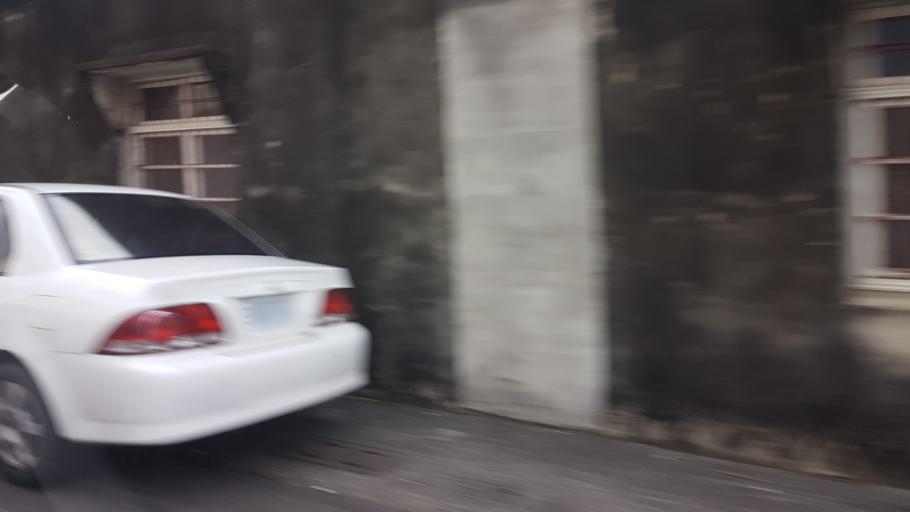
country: TW
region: Taiwan
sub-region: Chiayi
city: Jiayi Shi
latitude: 23.3831
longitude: 120.4389
